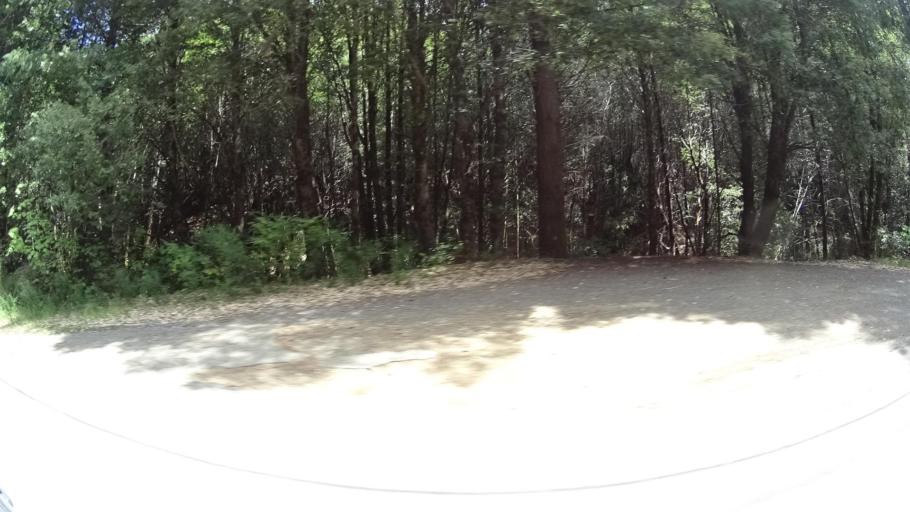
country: US
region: California
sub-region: Humboldt County
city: Redway
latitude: 40.0805
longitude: -123.9529
